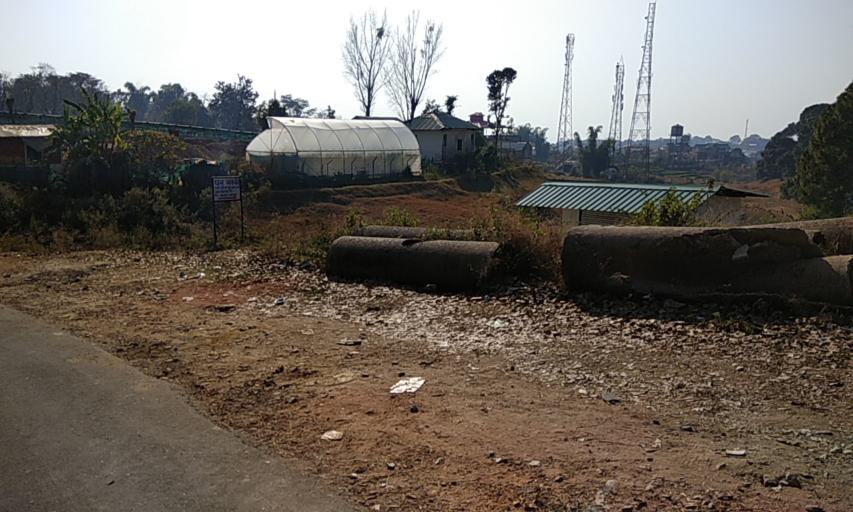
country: IN
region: Himachal Pradesh
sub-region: Kangra
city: Palampur
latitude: 32.1193
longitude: 76.5249
